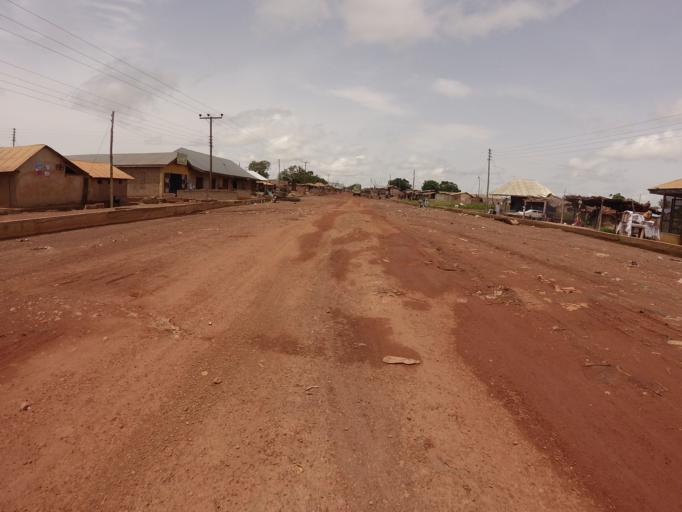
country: GH
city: Kpandae
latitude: 8.6962
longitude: 0.1761
